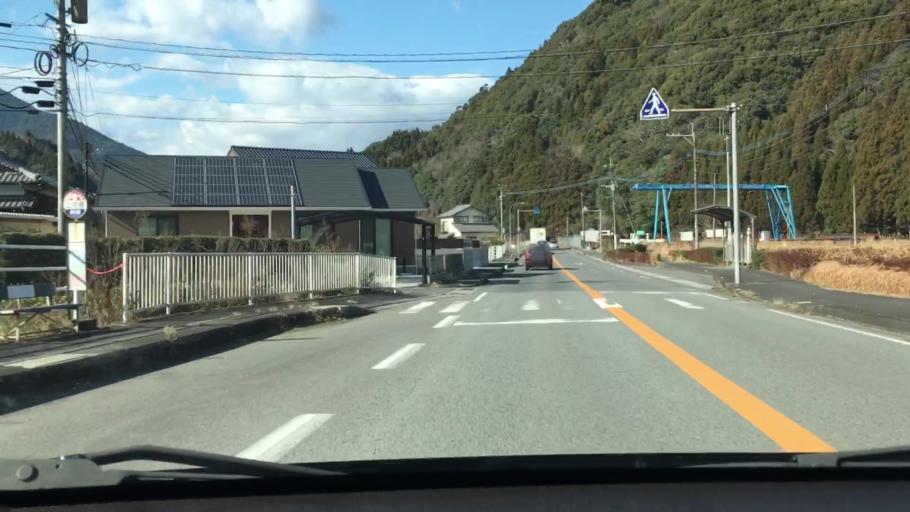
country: JP
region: Oita
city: Saiki
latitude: 32.9877
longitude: 131.8377
